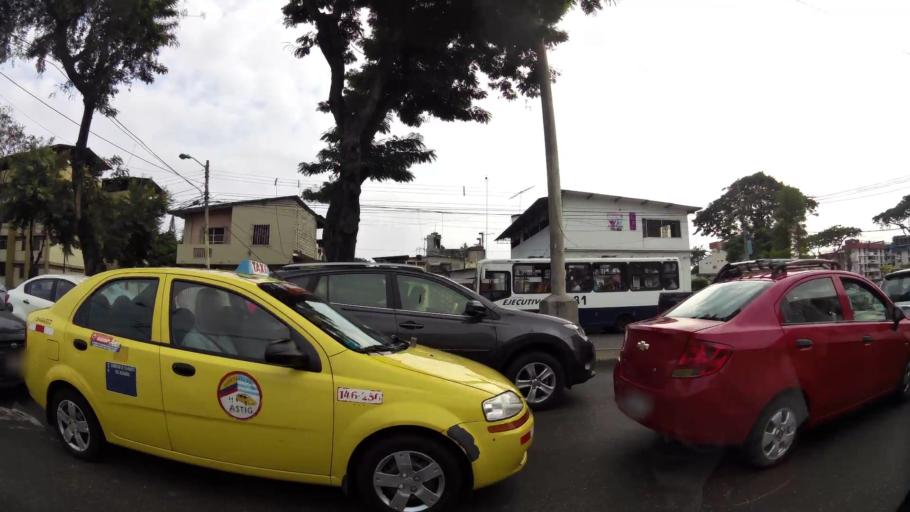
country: EC
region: Guayas
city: Guayaquil
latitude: -2.2391
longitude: -79.8921
